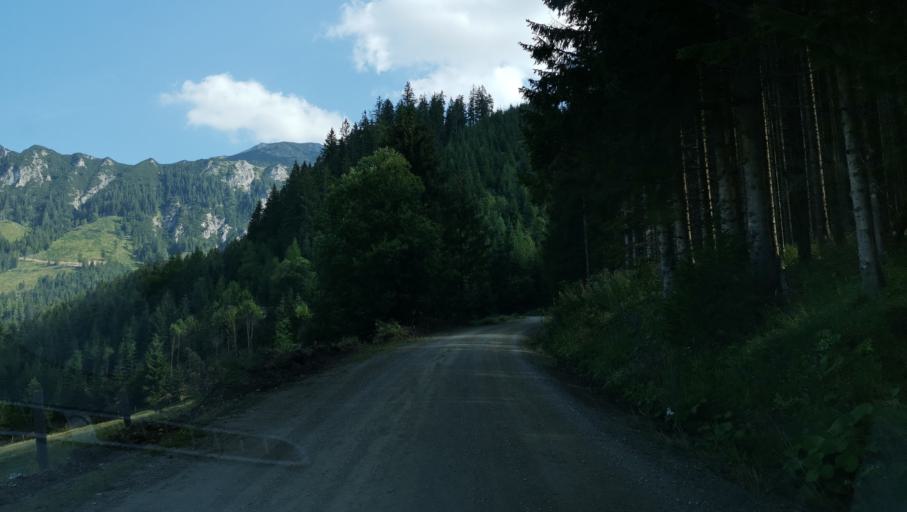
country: AT
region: Styria
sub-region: Politischer Bezirk Liezen
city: Trieben
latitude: 47.5304
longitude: 14.4897
